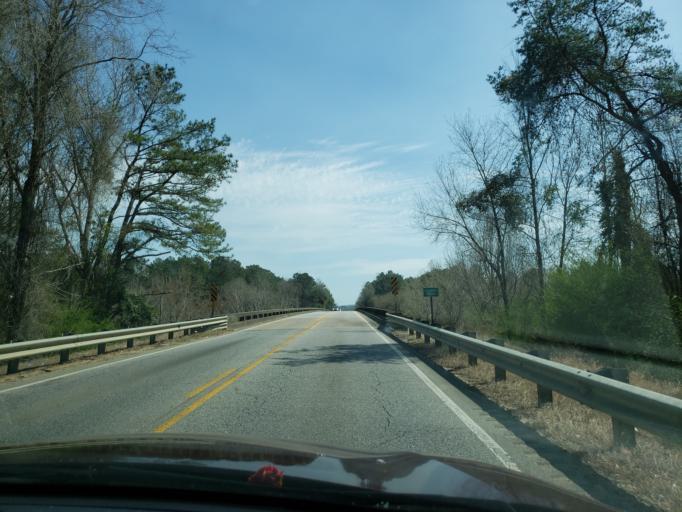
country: US
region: Alabama
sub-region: Elmore County
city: Elmore
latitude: 32.5418
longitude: -86.2703
